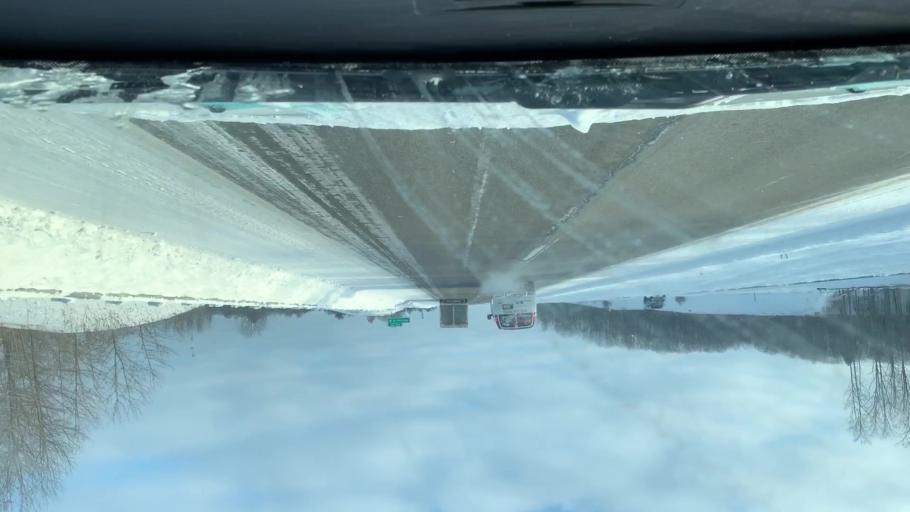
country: US
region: Michigan
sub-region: Wexford County
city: Cadillac
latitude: 44.2265
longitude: -85.3867
